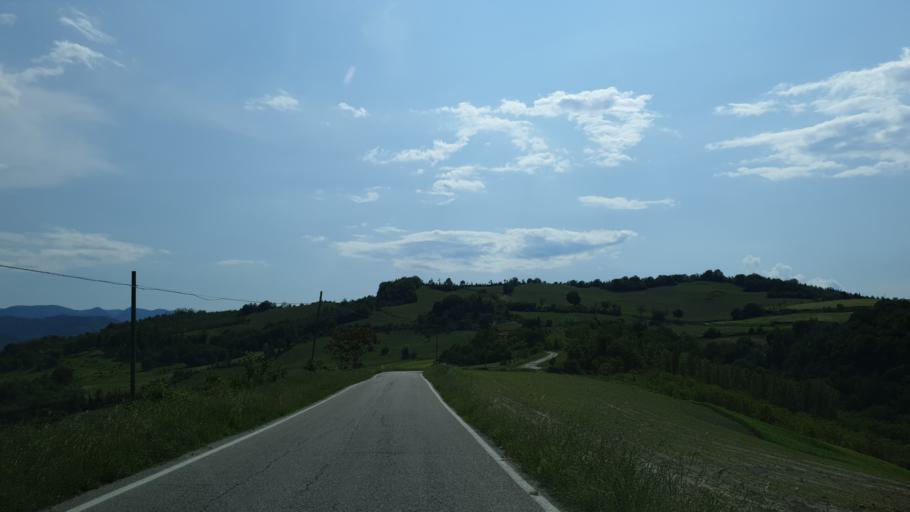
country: IT
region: Emilia-Romagna
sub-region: Forli-Cesena
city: Sarsina
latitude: 43.9085
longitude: 12.1840
